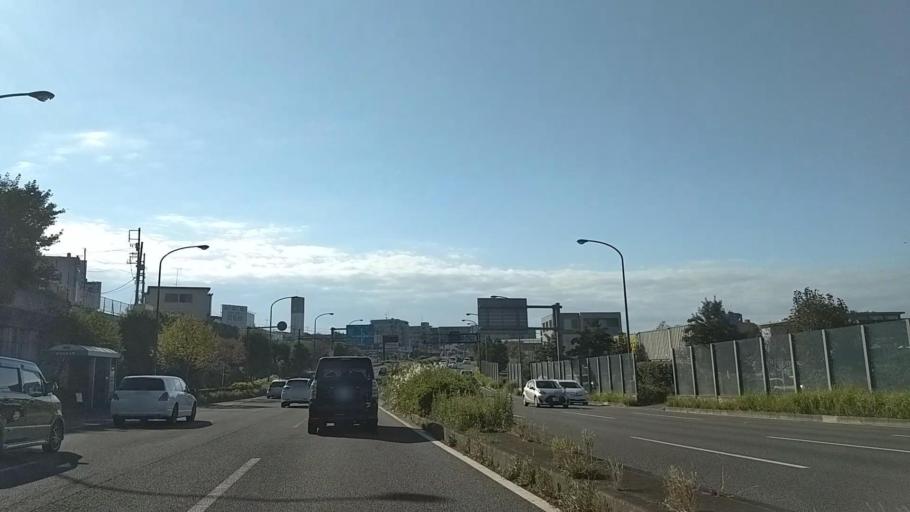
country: JP
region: Kanagawa
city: Yokohama
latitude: 35.4569
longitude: 139.5632
